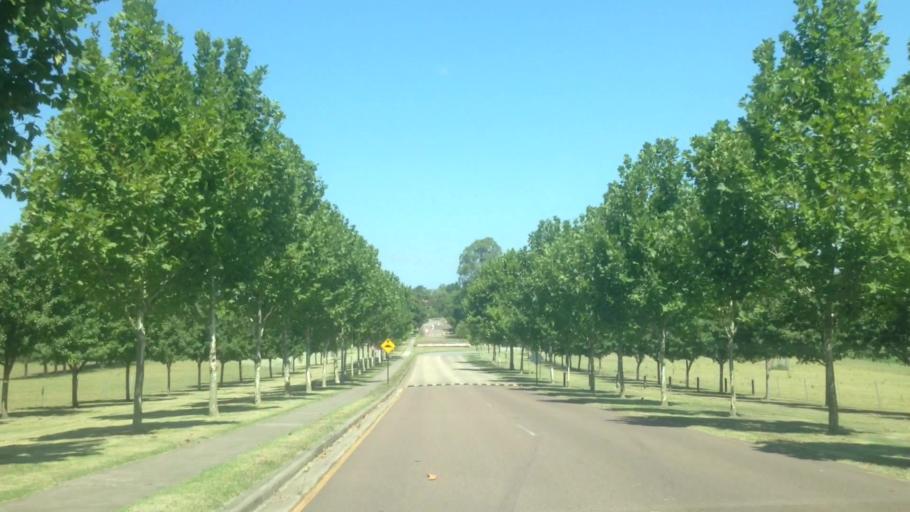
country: AU
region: New South Wales
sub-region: Lake Macquarie Shire
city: Cooranbong
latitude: -33.0835
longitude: 151.4576
